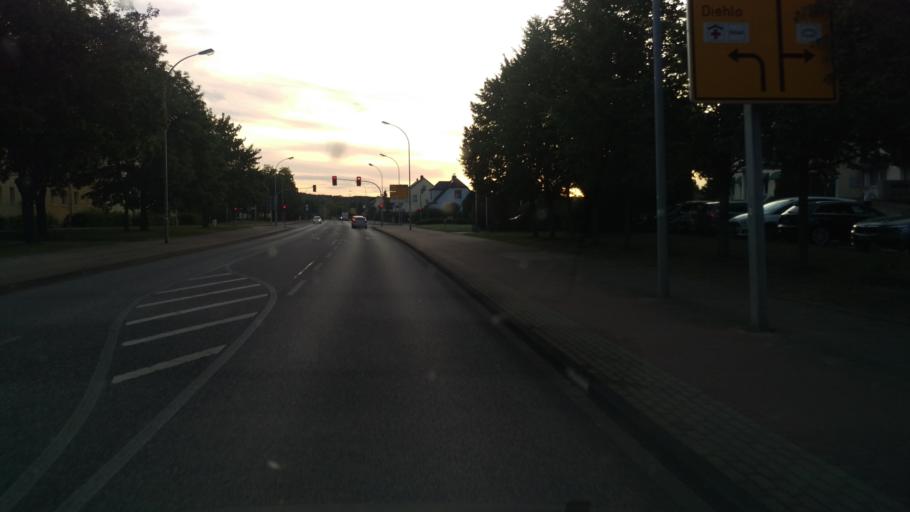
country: DE
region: Brandenburg
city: Eisenhuettenstadt
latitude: 52.1524
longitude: 14.6289
